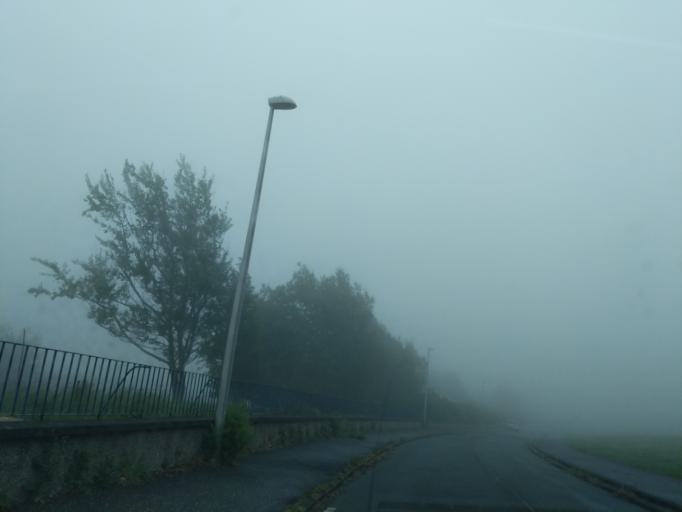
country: GB
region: Scotland
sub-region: West Lothian
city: Seafield
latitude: 55.9490
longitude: -3.1448
